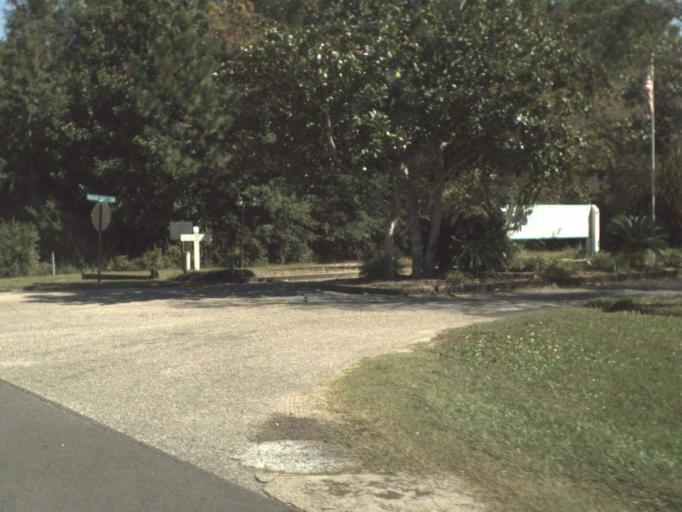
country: US
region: Florida
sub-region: Walton County
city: Miramar Beach
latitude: 30.4839
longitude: -86.2813
